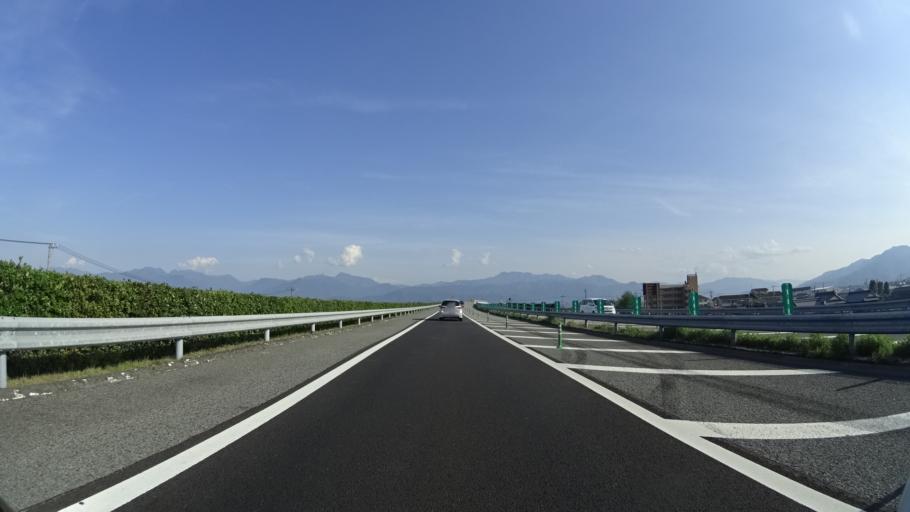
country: JP
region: Ehime
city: Saijo
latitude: 33.9545
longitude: 133.0682
